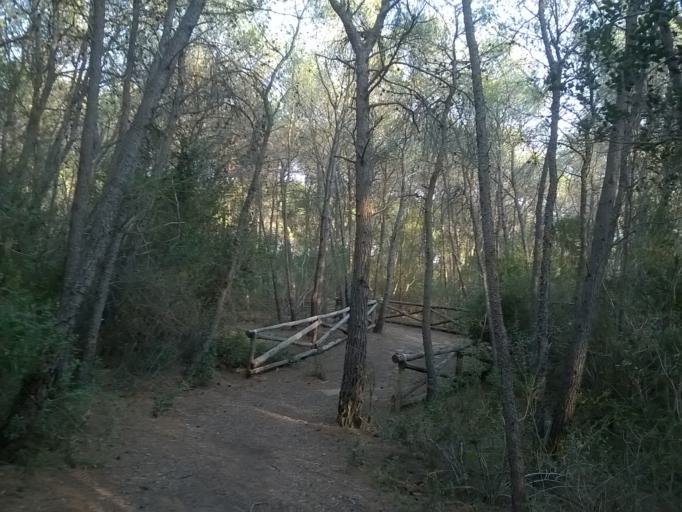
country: IT
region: Apulia
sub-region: Provincia di Taranto
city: Marina di Ginosa
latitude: 40.4708
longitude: 16.9454
